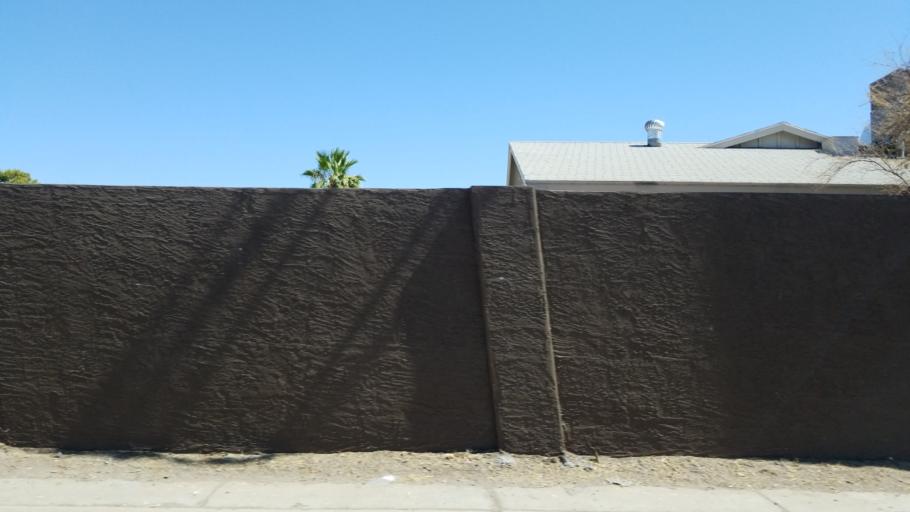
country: US
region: Arizona
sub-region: Maricopa County
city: Tolleson
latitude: 33.4944
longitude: -112.2399
